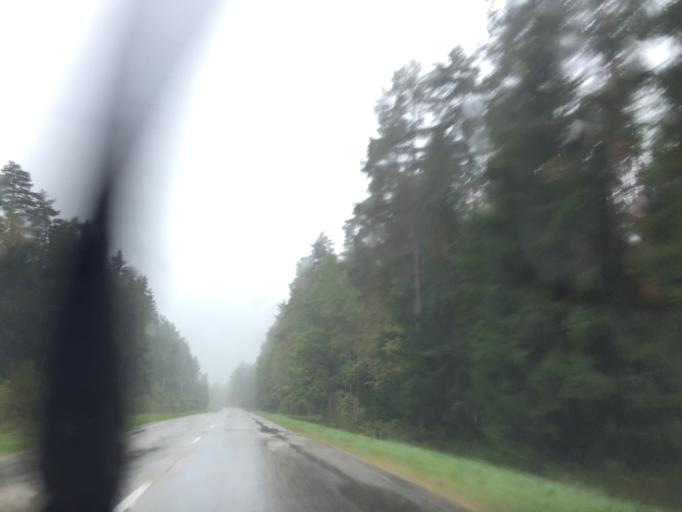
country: LV
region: Ropazu
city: Ropazi
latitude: 56.9851
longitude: 24.6344
